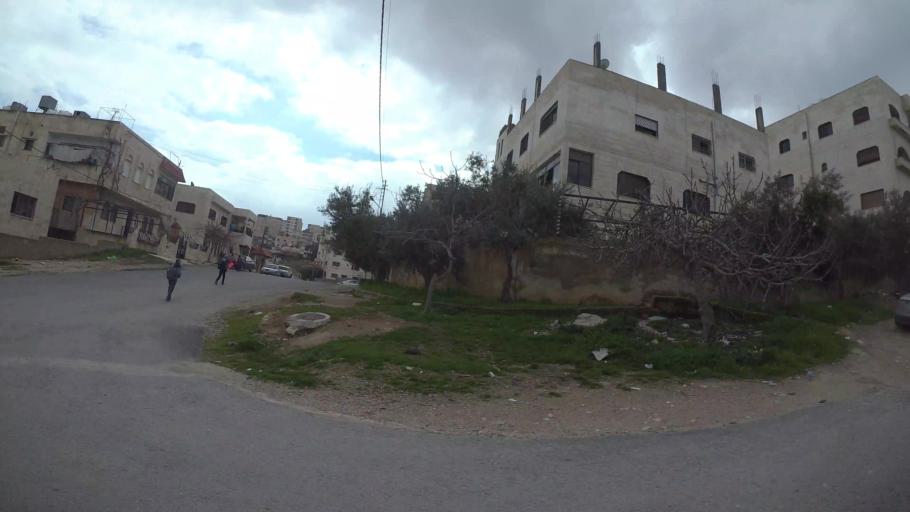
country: JO
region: Amman
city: Al Jubayhah
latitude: 32.0377
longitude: 35.8258
